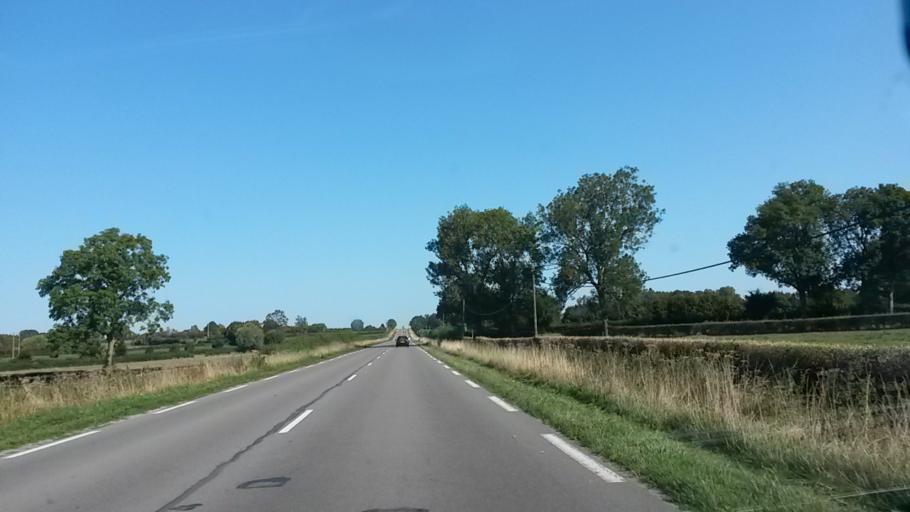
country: FR
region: Nord-Pas-de-Calais
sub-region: Departement du Nord
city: Avesnes-sur-Helpe
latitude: 50.0984
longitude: 3.9308
